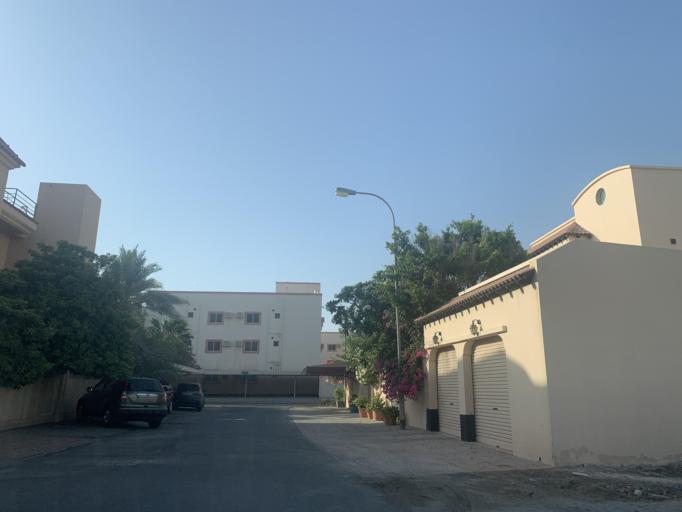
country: BH
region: Manama
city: Jidd Hafs
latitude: 26.2110
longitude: 50.5325
